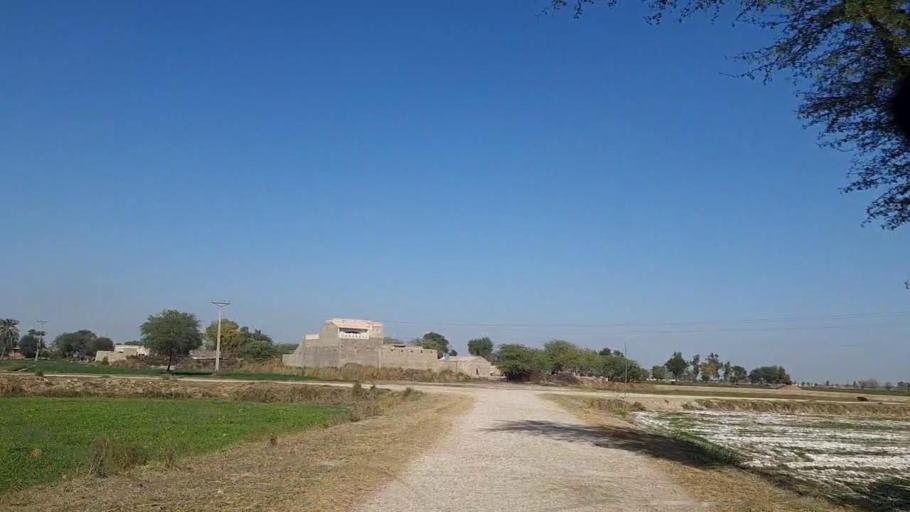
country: PK
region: Sindh
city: Khanpur
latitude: 27.8490
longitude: 69.3943
